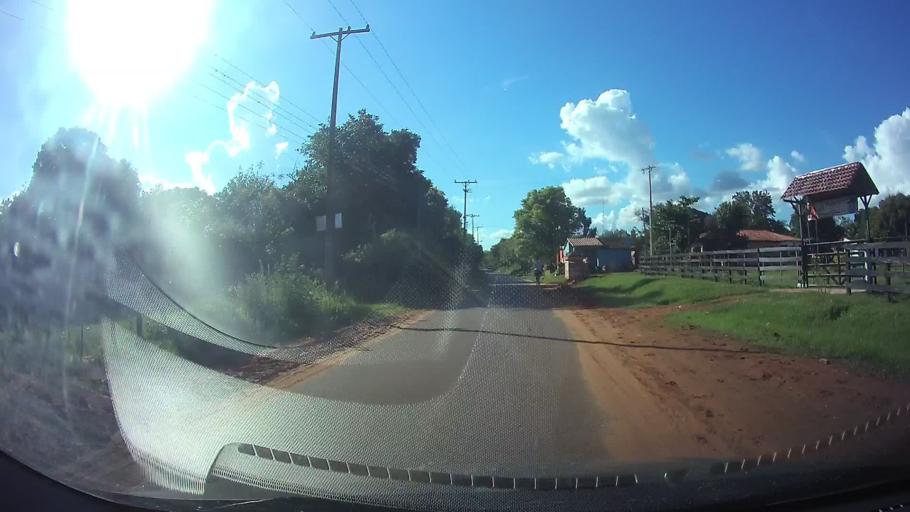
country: PY
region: Central
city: Itaugua
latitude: -25.3641
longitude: -57.3752
